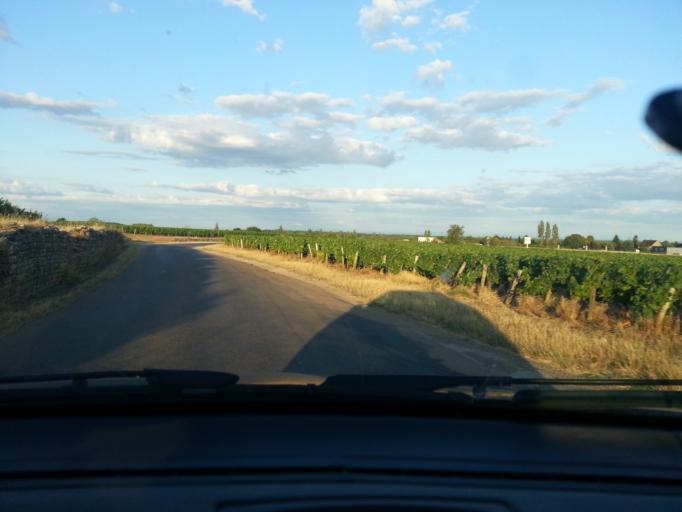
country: FR
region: Bourgogne
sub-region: Departement de Saone-et-Loire
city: Givry
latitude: 46.7581
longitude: 4.7122
